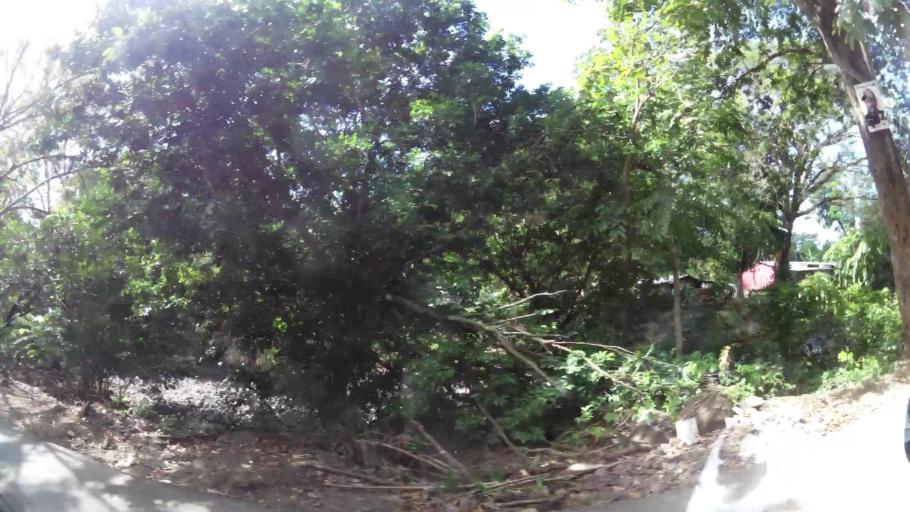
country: CR
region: Guanacaste
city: Juntas
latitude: 10.2816
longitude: -84.9485
